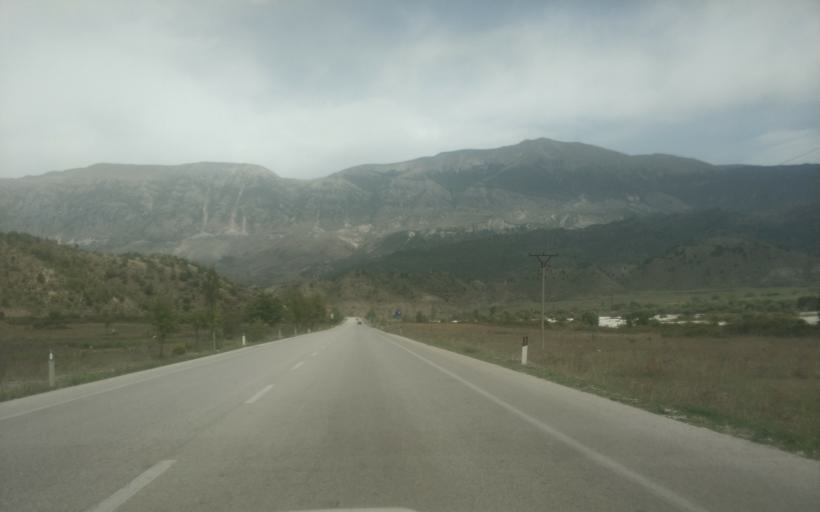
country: AL
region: Gjirokaster
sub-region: Rrethi i Gjirokastres
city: Picar
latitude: 40.1976
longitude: 20.0851
